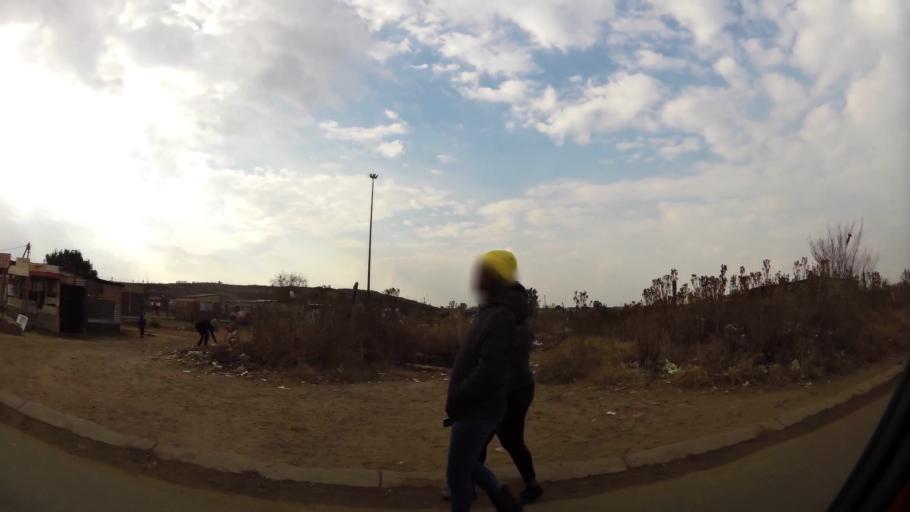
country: ZA
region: Gauteng
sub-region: Sedibeng District Municipality
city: Vanderbijlpark
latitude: -26.6747
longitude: 27.8588
